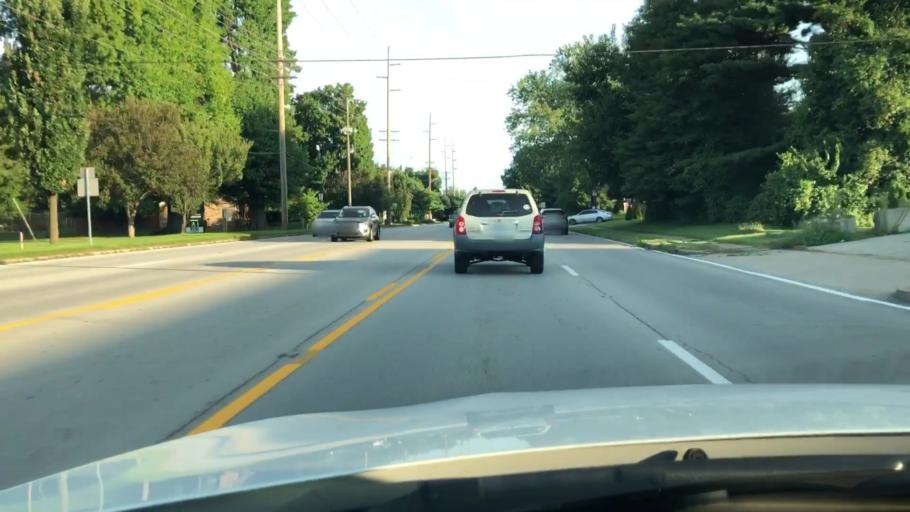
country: US
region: Kentucky
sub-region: Jefferson County
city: Saint Regis Park
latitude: 38.2219
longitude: -85.6322
